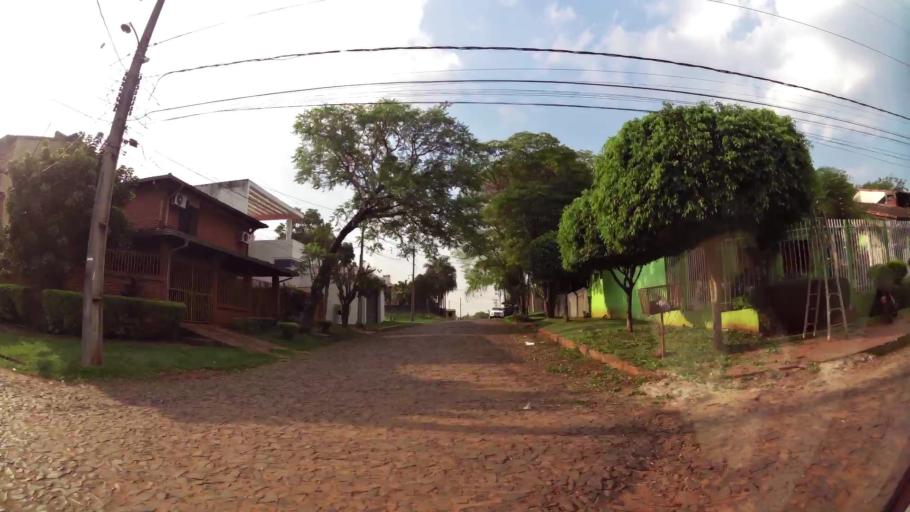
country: PY
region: Alto Parana
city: Presidente Franco
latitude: -25.5218
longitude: -54.6320
